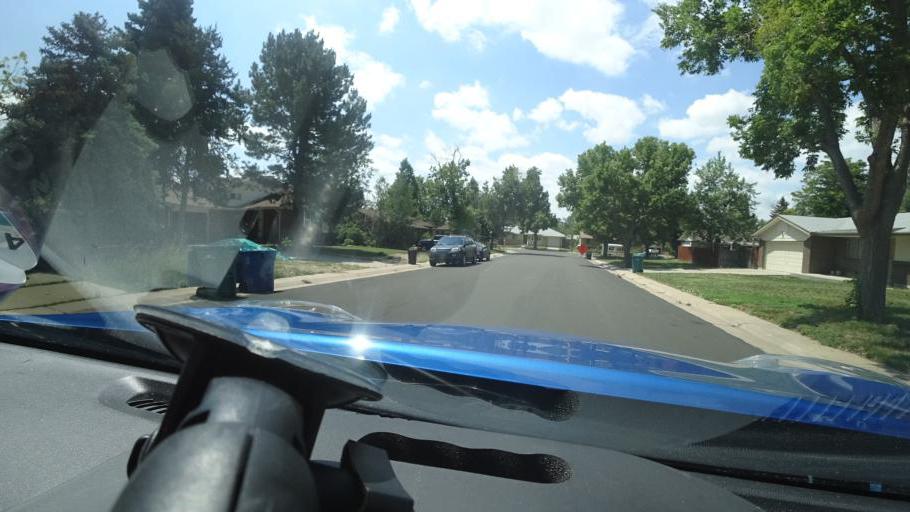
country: US
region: Colorado
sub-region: Adams County
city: Aurora
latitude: 39.7101
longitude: -104.8510
